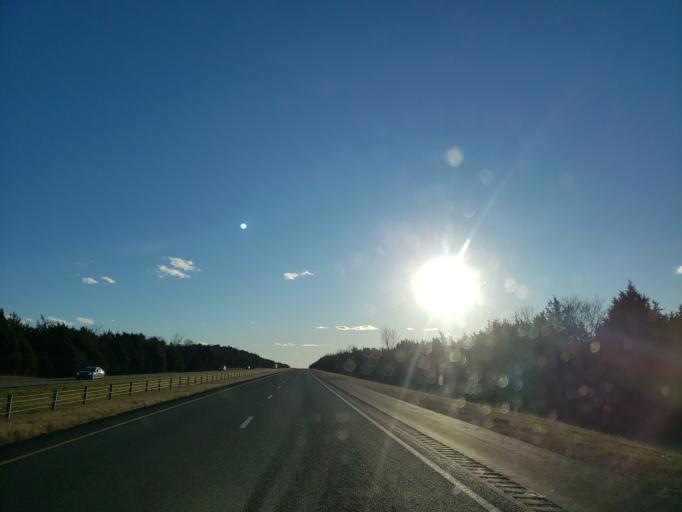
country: US
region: Alabama
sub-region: Sumter County
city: Livingston
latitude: 32.6677
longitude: -88.1756
